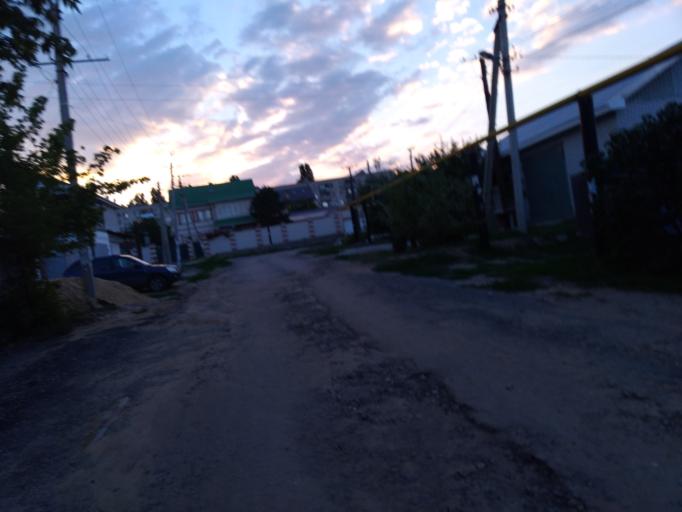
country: RU
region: Volgograd
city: Volgograd
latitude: 48.6703
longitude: 44.4511
